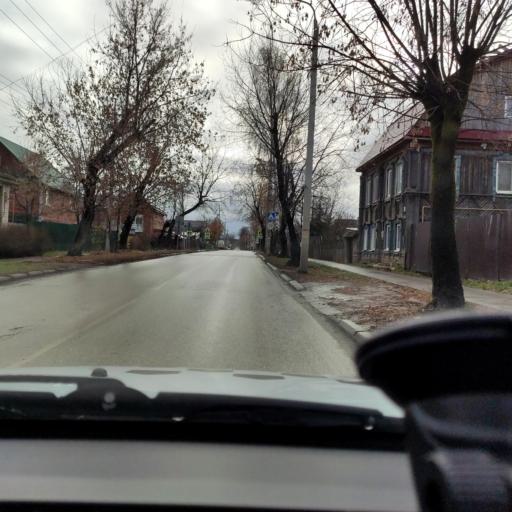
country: RU
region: Perm
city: Perm
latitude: 58.0276
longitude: 56.3311
